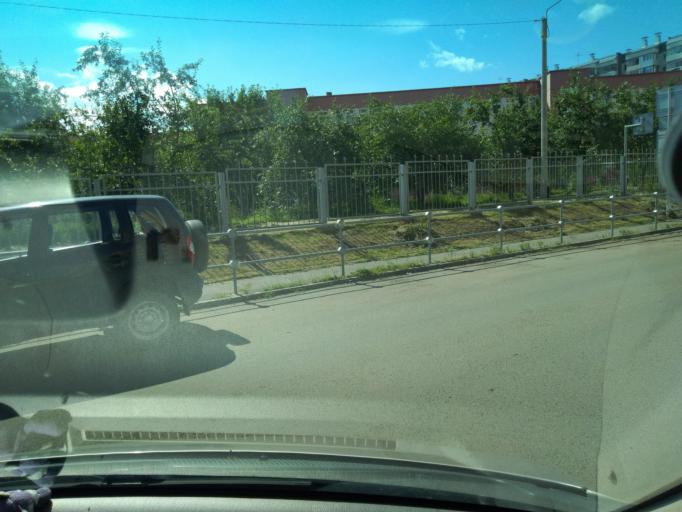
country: RU
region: Krasnoyarskiy
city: Krasnoyarsk
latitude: 56.0444
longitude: 92.9028
